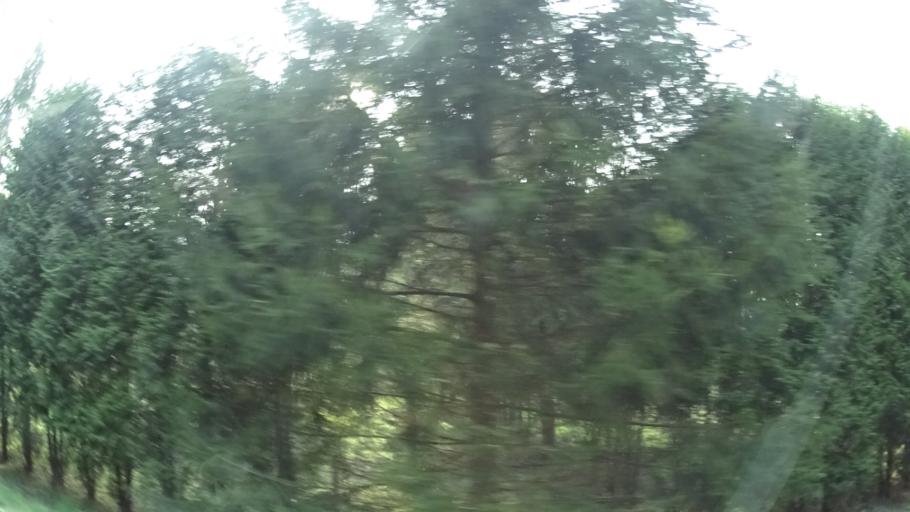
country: DE
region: Rheinland-Pfalz
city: Niederstaufenbach
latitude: 49.5381
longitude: 7.5098
